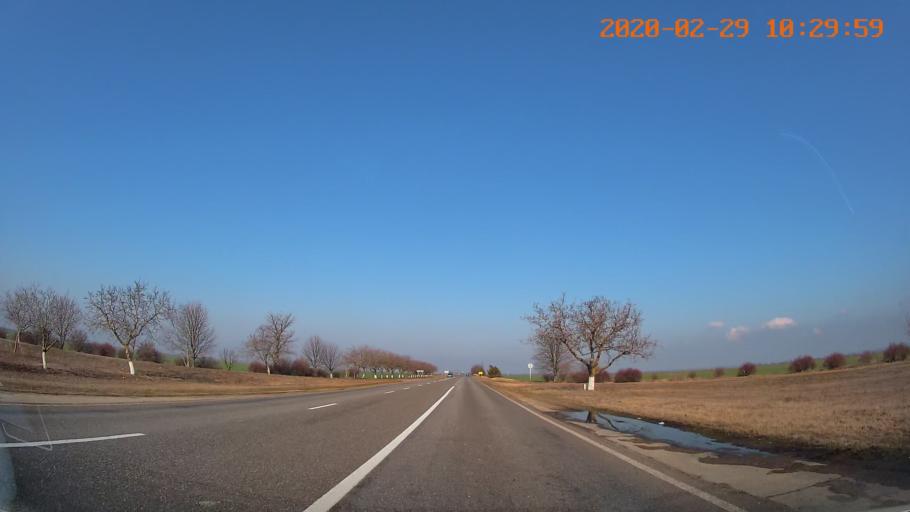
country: MD
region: Telenesti
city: Tiraspolul Nou
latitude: 46.9298
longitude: 29.5802
